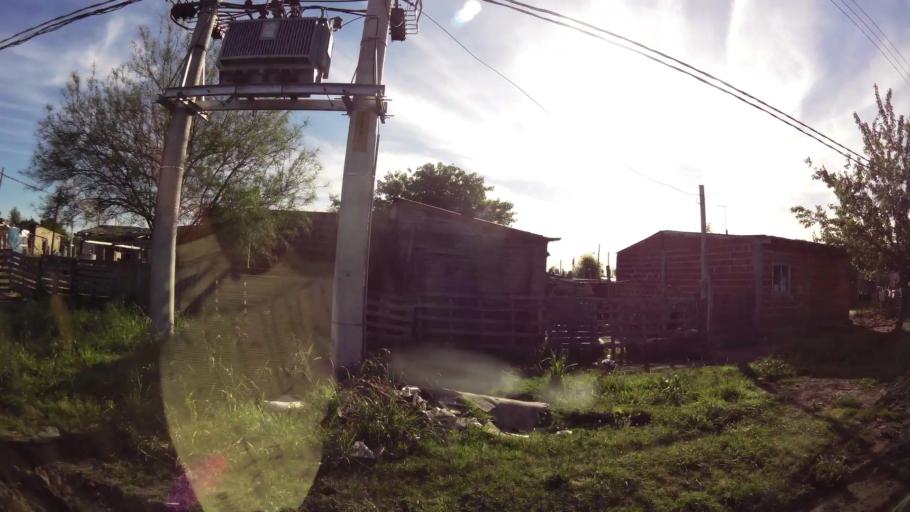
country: AR
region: Buenos Aires
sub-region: Partido de Almirante Brown
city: Adrogue
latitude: -34.8189
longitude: -58.3228
